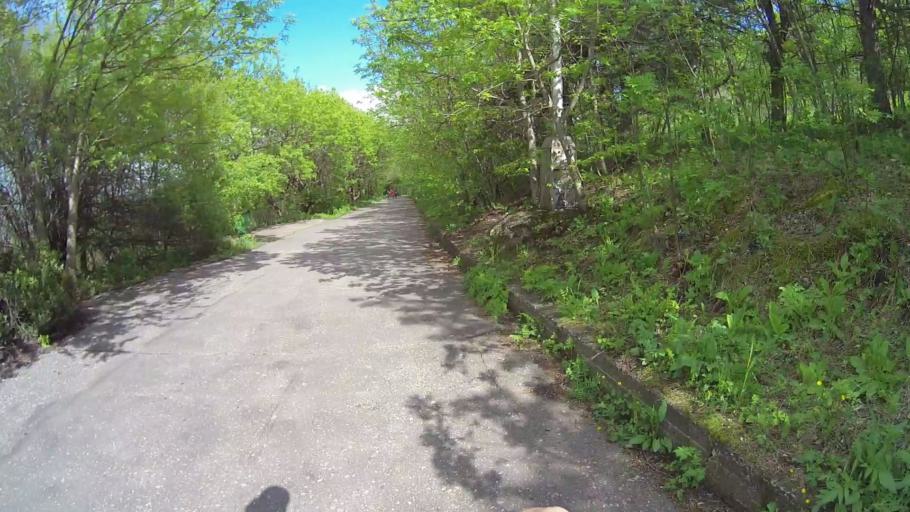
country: RU
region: Stavropol'skiy
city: Pyatigorsk
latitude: 44.0520
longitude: 43.0868
